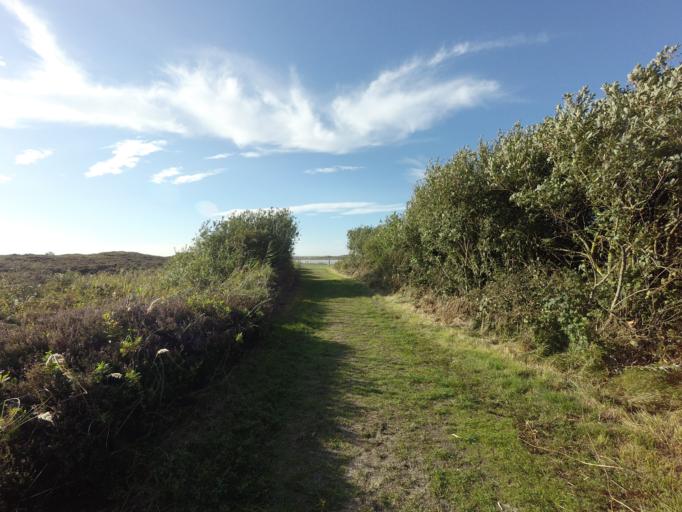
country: NL
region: North Holland
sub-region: Gemeente Den Helder
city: Den Helder
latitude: 53.0140
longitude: 4.7363
